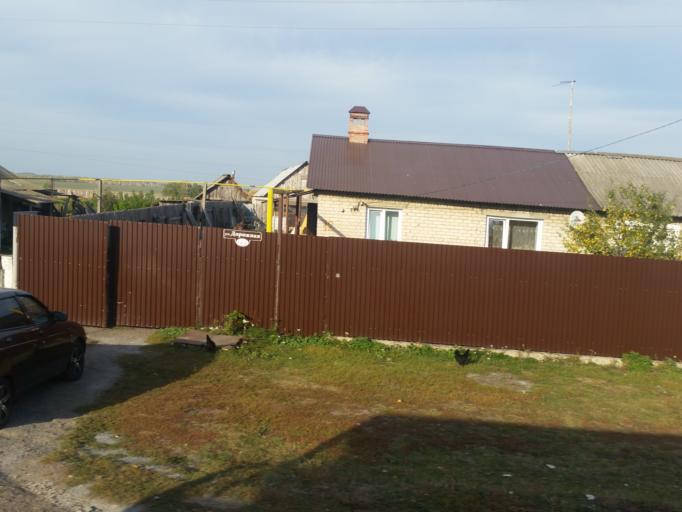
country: RU
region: Ulyanovsk
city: Mullovka
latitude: 54.2663
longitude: 49.1685
